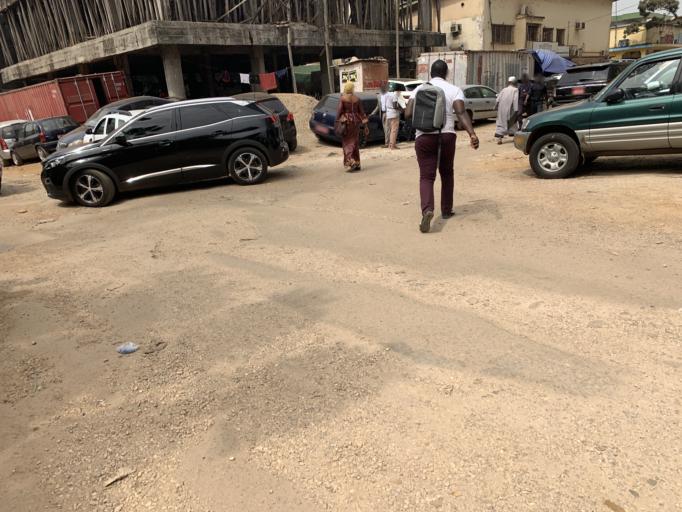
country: GN
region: Conakry
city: Camayenne
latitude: 9.5101
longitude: -13.7132
